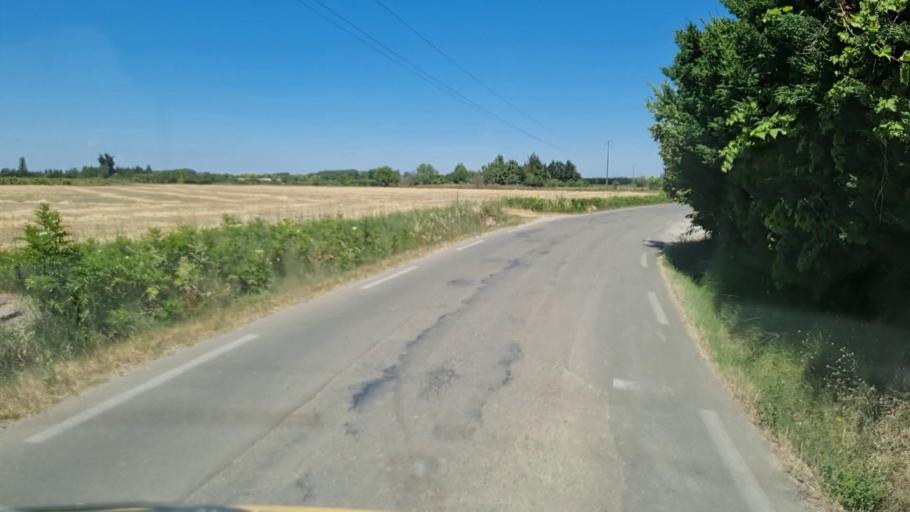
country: FR
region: Languedoc-Roussillon
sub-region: Departement de l'Herault
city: Marsillargues
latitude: 43.6726
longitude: 4.1853
